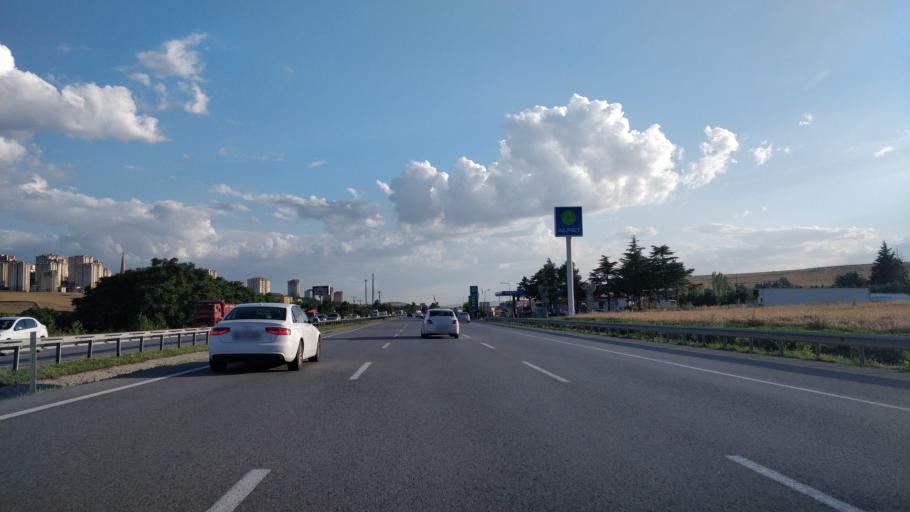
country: TR
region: Ankara
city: Etimesgut
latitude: 39.8278
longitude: 32.5771
